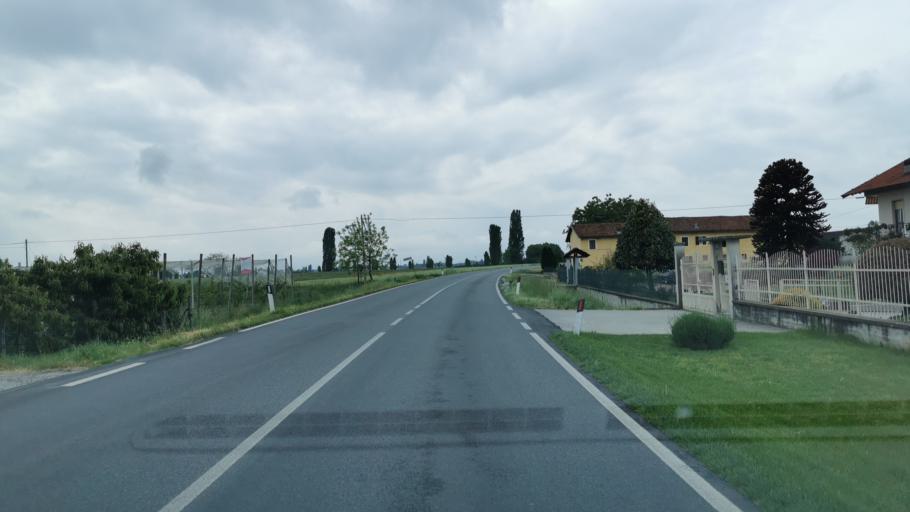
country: IT
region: Piedmont
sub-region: Provincia di Cuneo
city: Villafalletto
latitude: 44.5703
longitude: 7.5295
